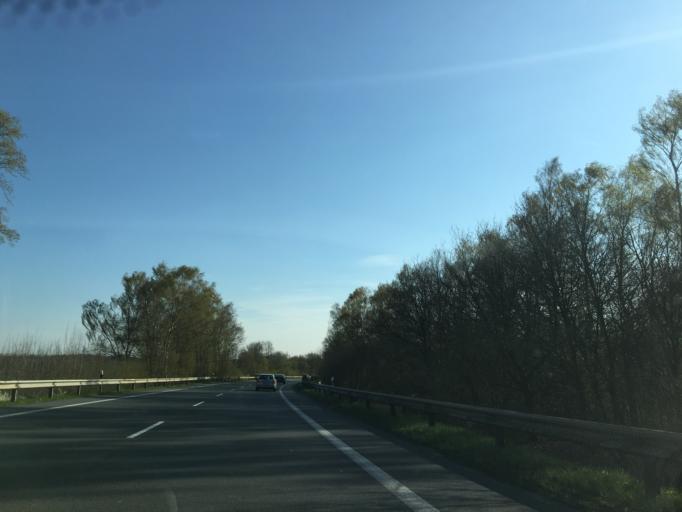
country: DE
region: North Rhine-Westphalia
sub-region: Regierungsbezirk Munster
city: Muenster
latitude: 52.0411
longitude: 7.6858
